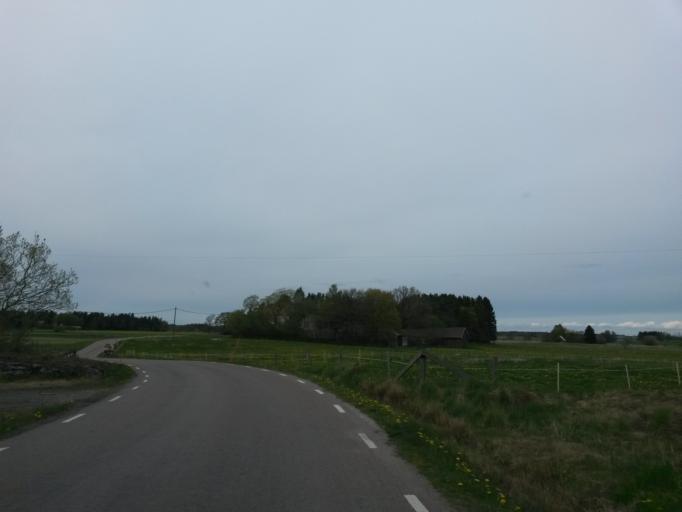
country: SE
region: Vaestra Goetaland
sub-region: Grastorps Kommun
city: Graestorp
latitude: 58.3370
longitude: 12.7636
